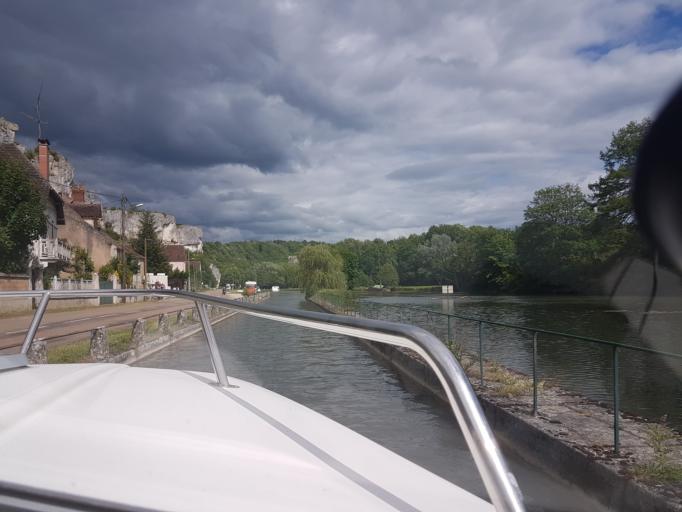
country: FR
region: Bourgogne
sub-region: Departement de l'Yonne
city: Vermenton
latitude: 47.5659
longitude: 3.6432
